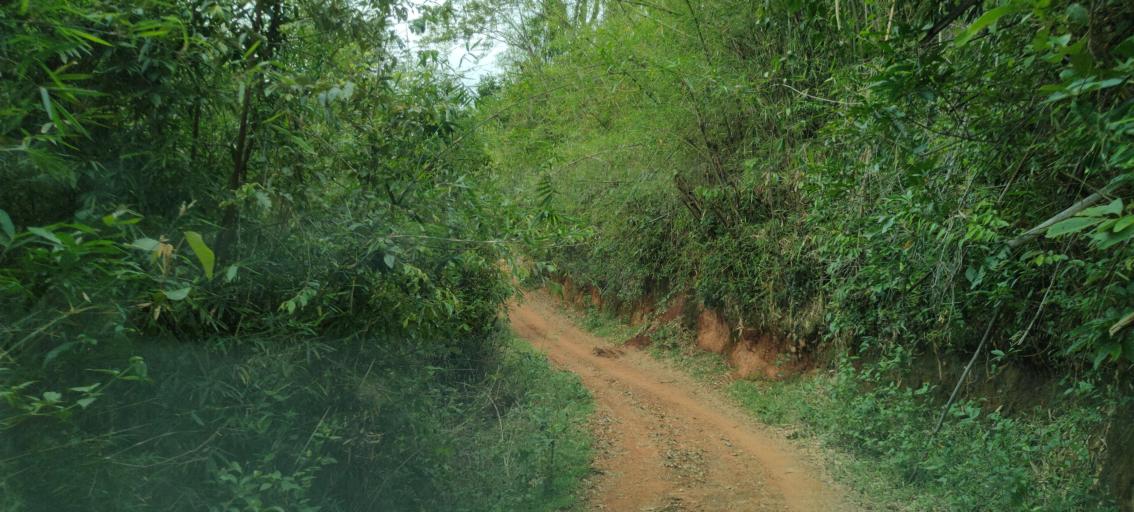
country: LA
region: Loungnamtha
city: Muang Nale
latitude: 20.4345
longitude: 101.4754
